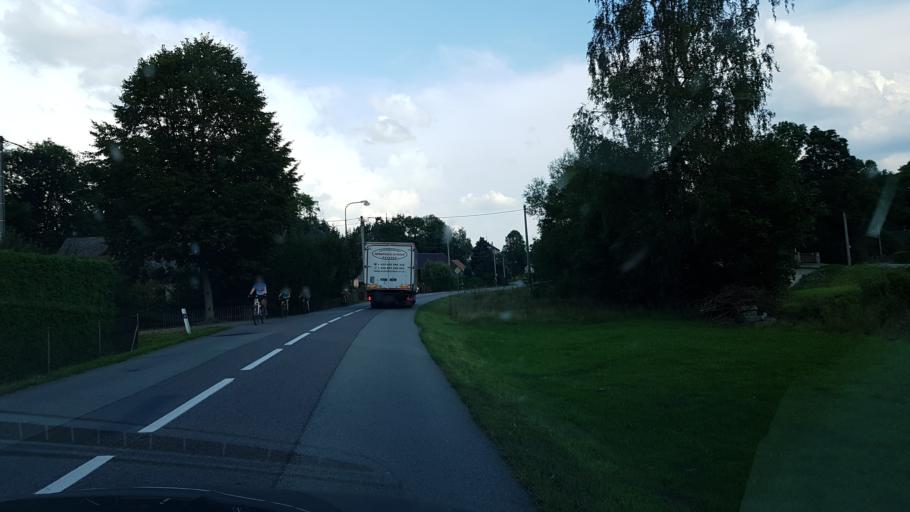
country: CZ
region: Pardubicky
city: Lukavice
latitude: 50.0824
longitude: 16.5032
